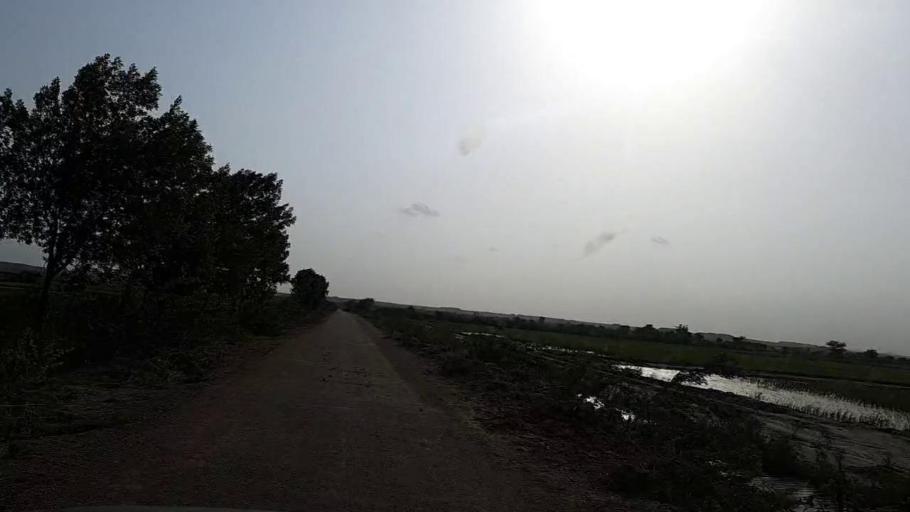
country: PK
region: Sindh
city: Kotri
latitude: 25.1858
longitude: 68.2550
